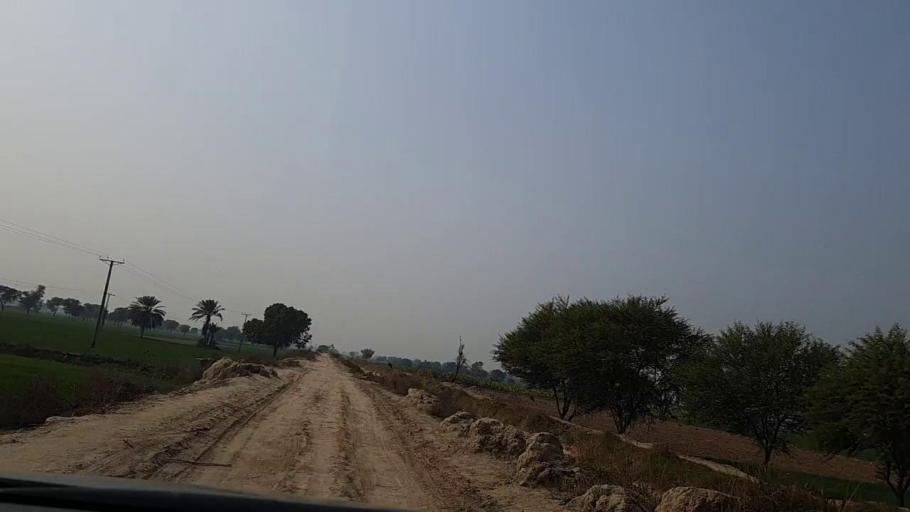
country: PK
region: Sindh
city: Sakrand
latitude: 26.1392
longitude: 68.2307
